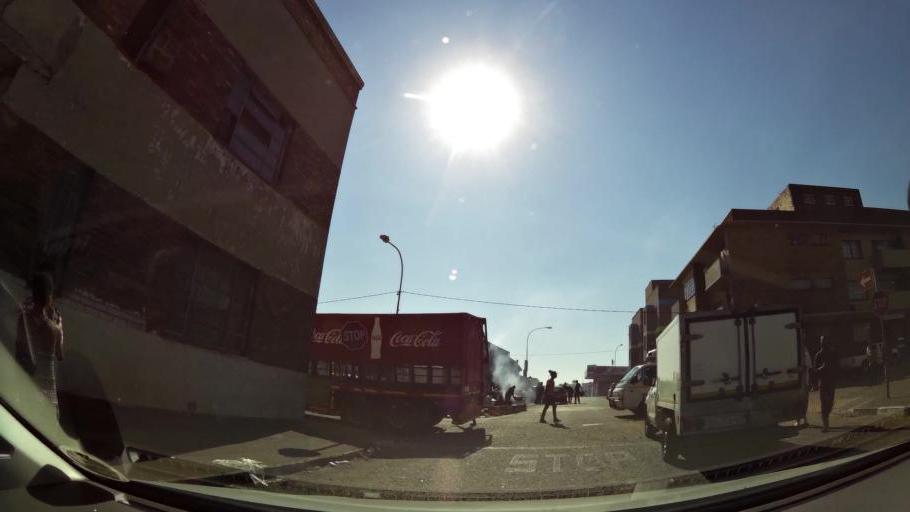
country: ZA
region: Gauteng
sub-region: City of Johannesburg Metropolitan Municipality
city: Johannesburg
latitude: -26.2036
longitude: 28.0647
